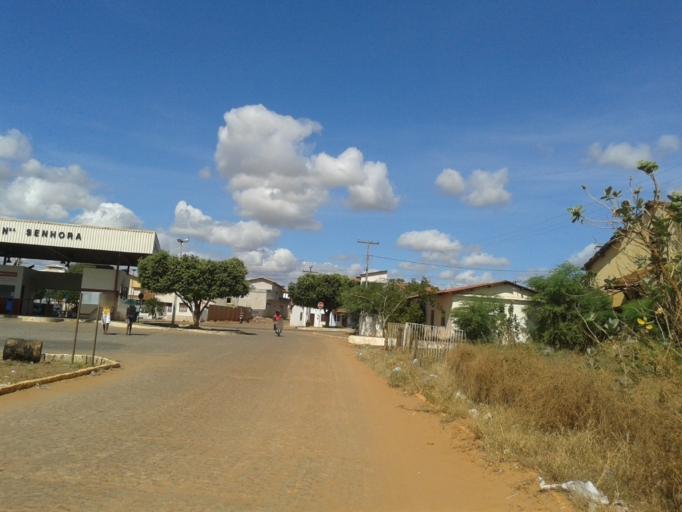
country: BR
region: Bahia
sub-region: Livramento Do Brumado
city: Livramento do Brumado
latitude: -13.6563
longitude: -41.8484
